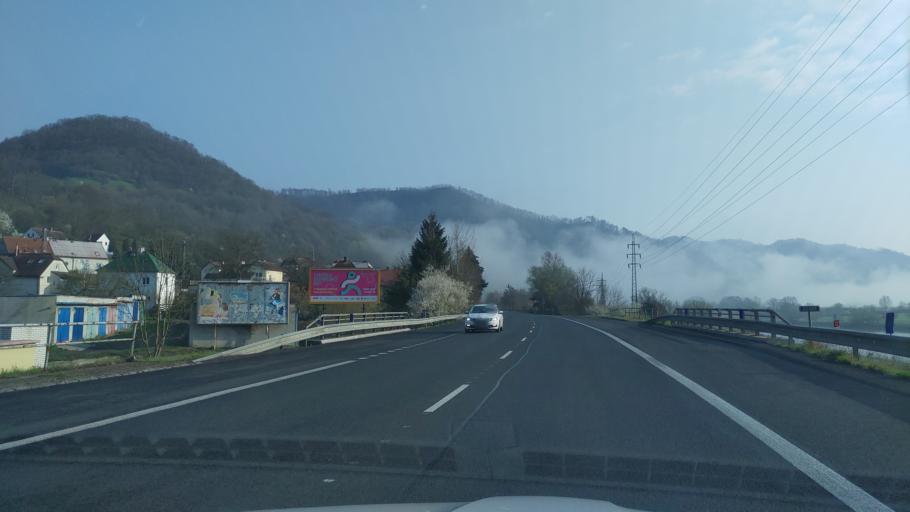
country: CZ
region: Ustecky
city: Povrly
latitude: 50.6727
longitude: 14.1644
